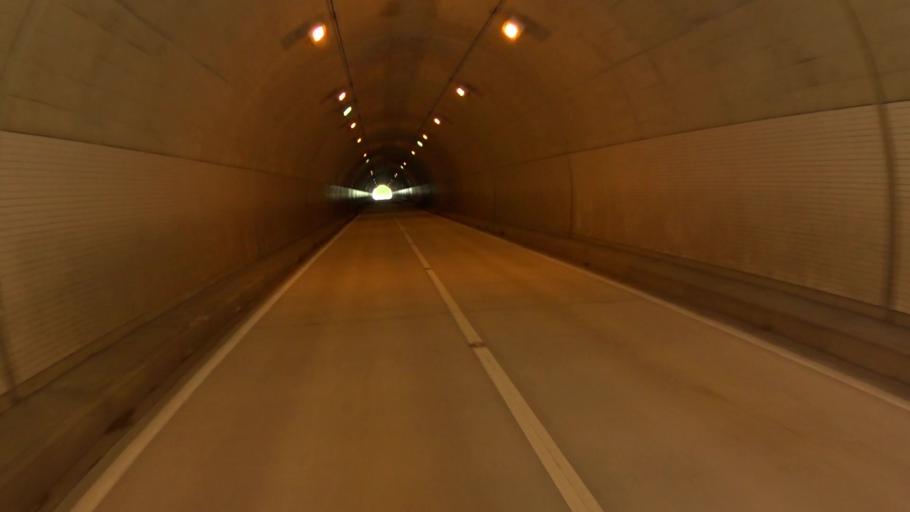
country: JP
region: Kyoto
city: Kameoka
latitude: 35.1126
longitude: 135.5636
